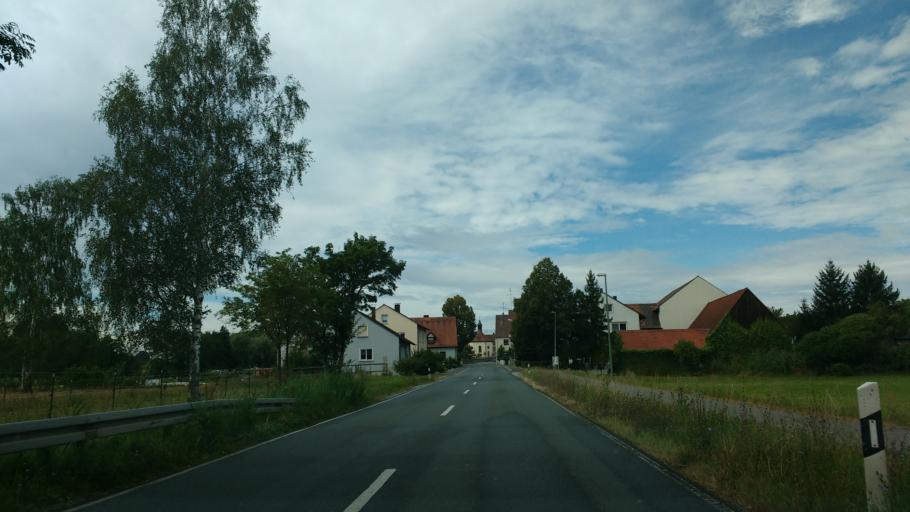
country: DE
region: Bavaria
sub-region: Upper Franconia
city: Schlusselfeld
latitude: 49.7590
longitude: 10.6118
